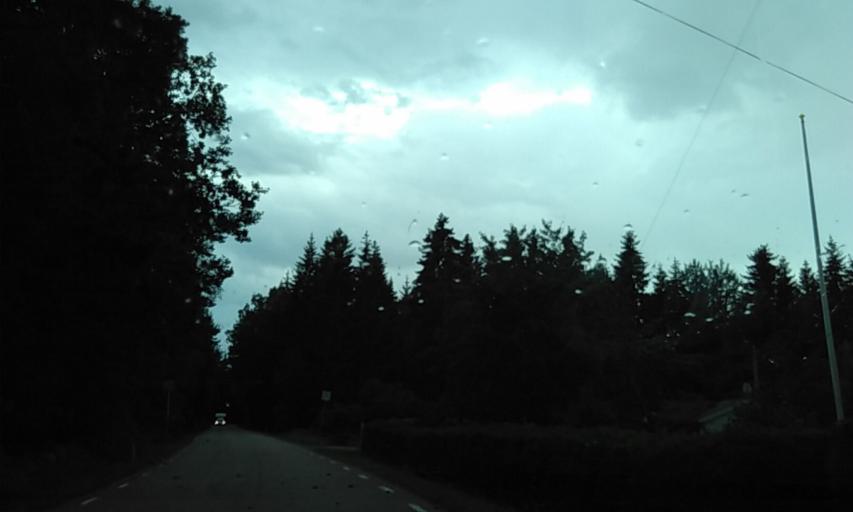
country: SE
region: Vaestra Goetaland
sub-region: Grastorps Kommun
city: Graestorp
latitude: 58.4589
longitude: 12.7976
